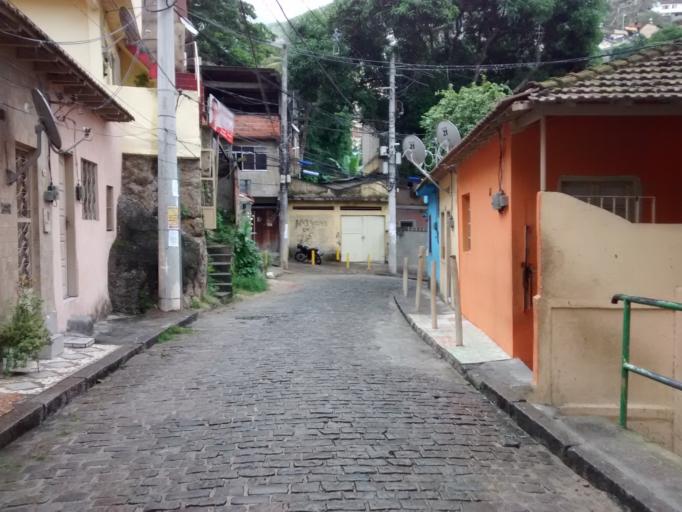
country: BR
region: Rio de Janeiro
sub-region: Rio De Janeiro
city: Rio de Janeiro
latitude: -22.9332
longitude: -43.2569
